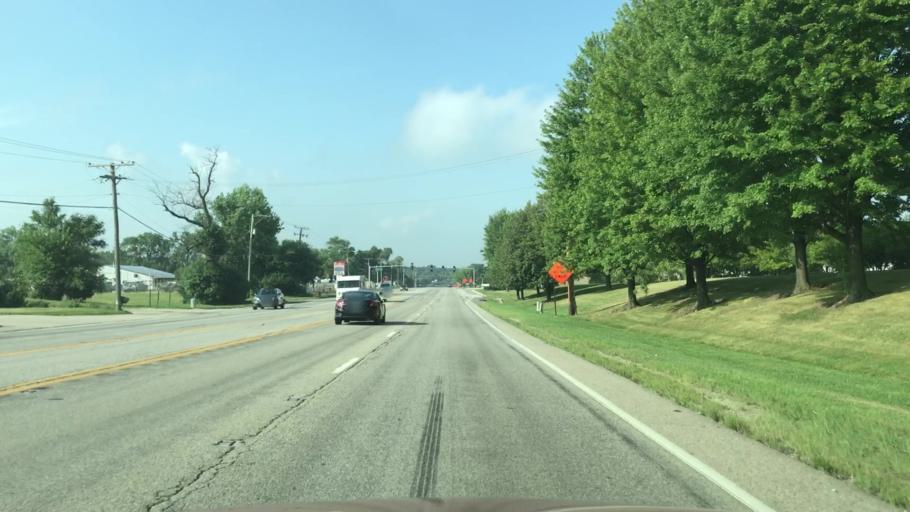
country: US
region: Illinois
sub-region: Will County
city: Bolingbrook
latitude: 41.6821
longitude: -88.0521
